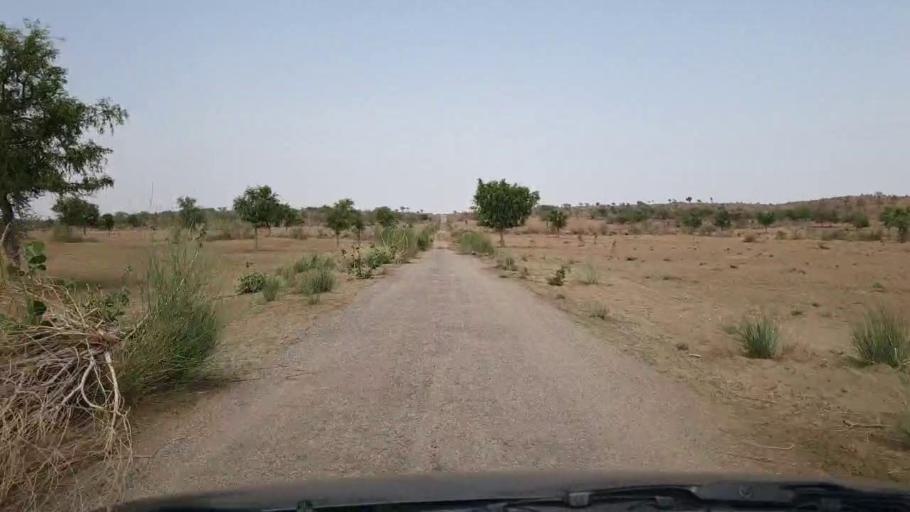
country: PK
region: Sindh
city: Chor
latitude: 25.4817
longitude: 70.5485
